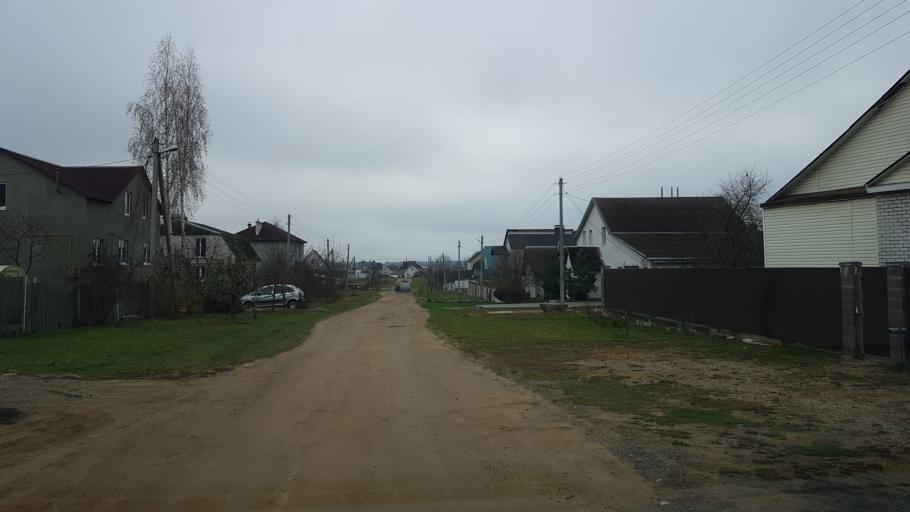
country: BY
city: Fanipol
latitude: 53.7329
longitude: 27.3142
